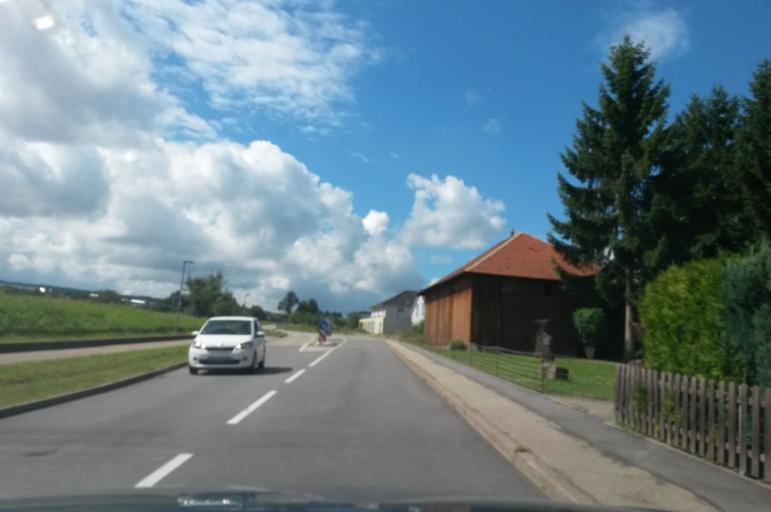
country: DE
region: Baden-Wuerttemberg
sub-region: Karlsruhe Region
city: Dobel
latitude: 48.8526
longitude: 8.5270
